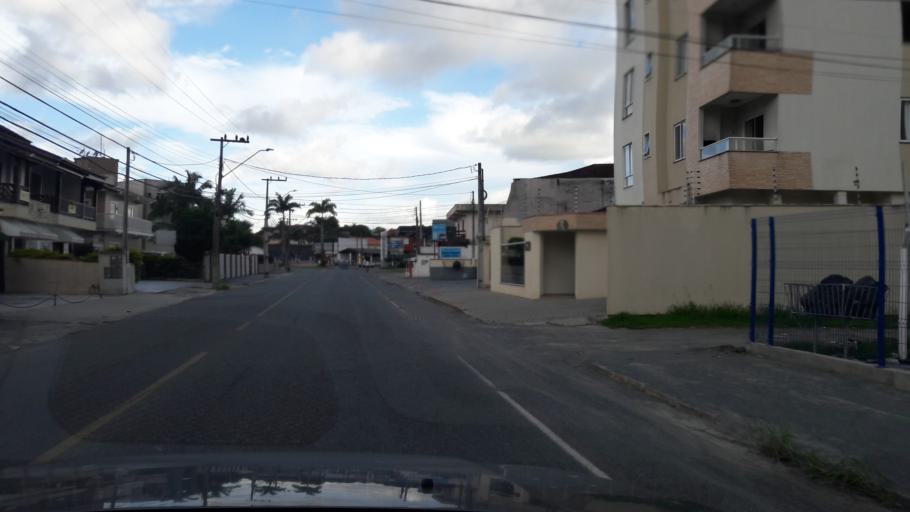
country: BR
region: Santa Catarina
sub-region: Joinville
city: Joinville
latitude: -26.3257
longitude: -48.8325
